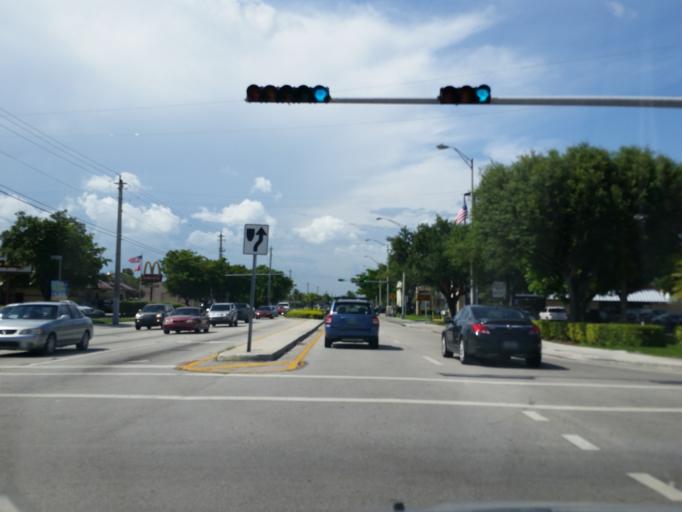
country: US
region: Florida
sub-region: Miami-Dade County
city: Westchester
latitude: 25.7477
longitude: -80.3356
